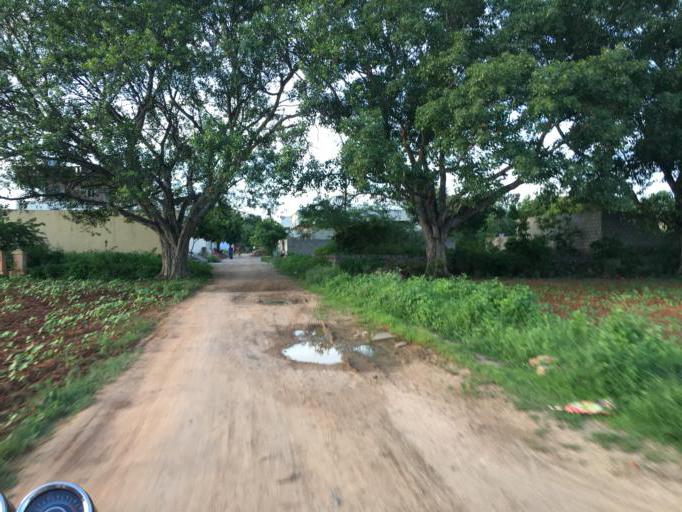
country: IN
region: Telangana
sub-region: Nalgonda
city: Nalgonda
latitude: 17.1728
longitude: 79.4176
